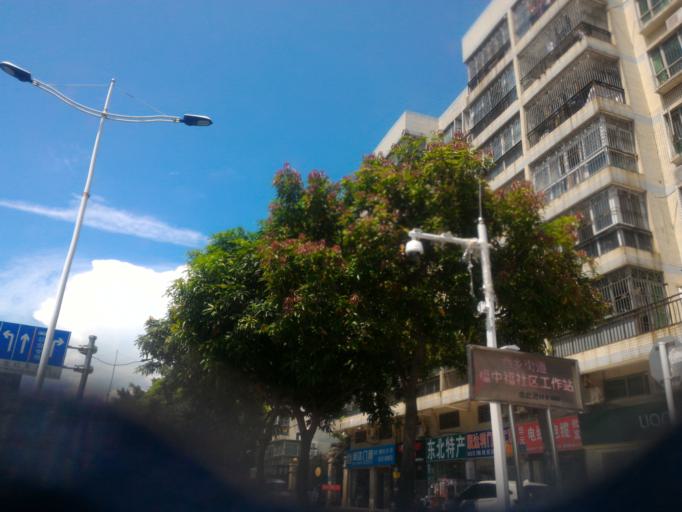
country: CN
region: Guangdong
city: Xixiang
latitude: 22.5667
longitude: 113.8693
